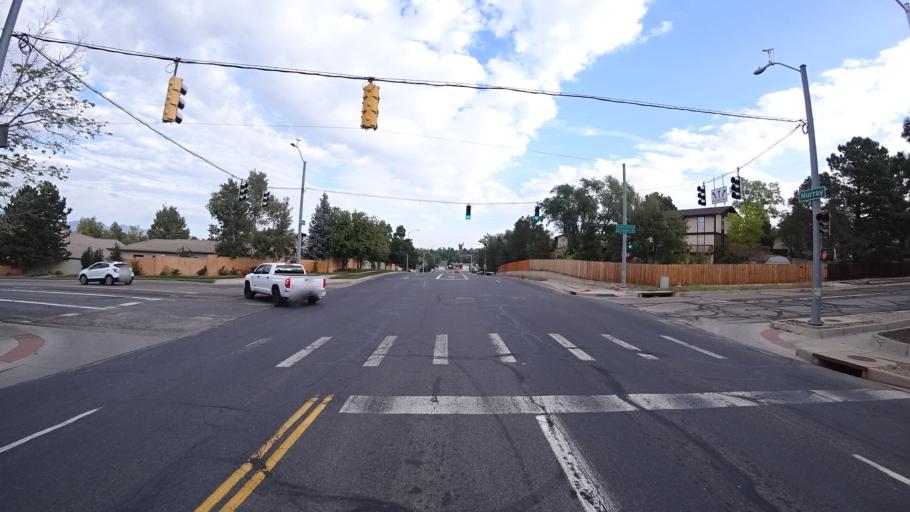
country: US
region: Colorado
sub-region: El Paso County
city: Cimarron Hills
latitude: 38.8718
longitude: -104.7479
